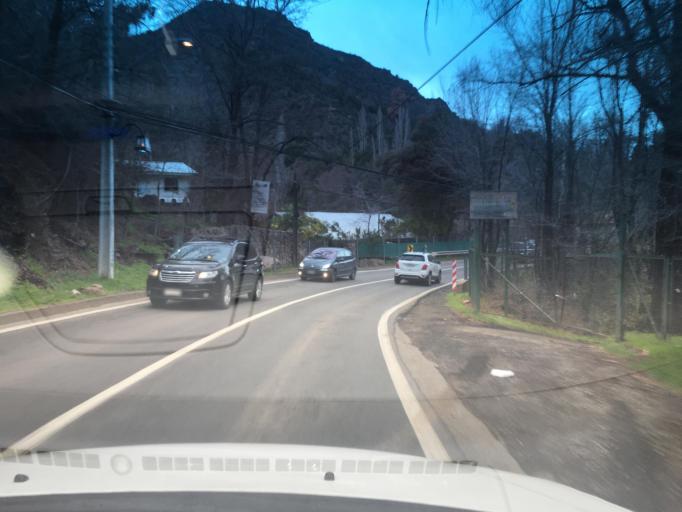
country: CL
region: Santiago Metropolitan
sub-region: Provincia de Cordillera
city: Puente Alto
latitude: -33.6562
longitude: -70.3498
